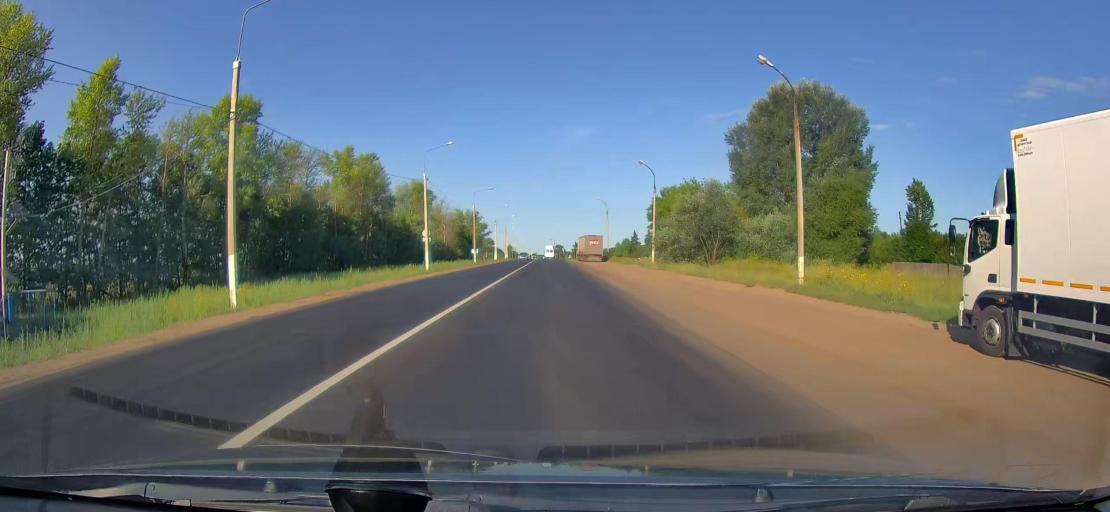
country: RU
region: Tula
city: Bol'shoye Skuratovo
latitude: 53.4345
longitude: 36.8077
